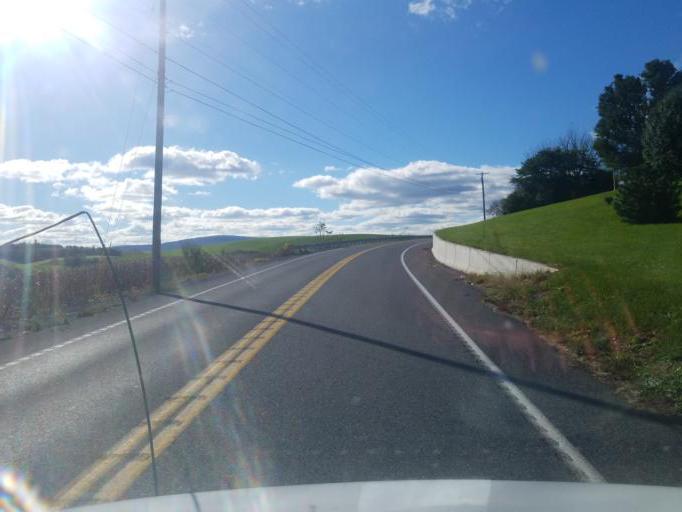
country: US
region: Pennsylvania
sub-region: Franklin County
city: Waynesboro
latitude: 39.7821
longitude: -77.5695
